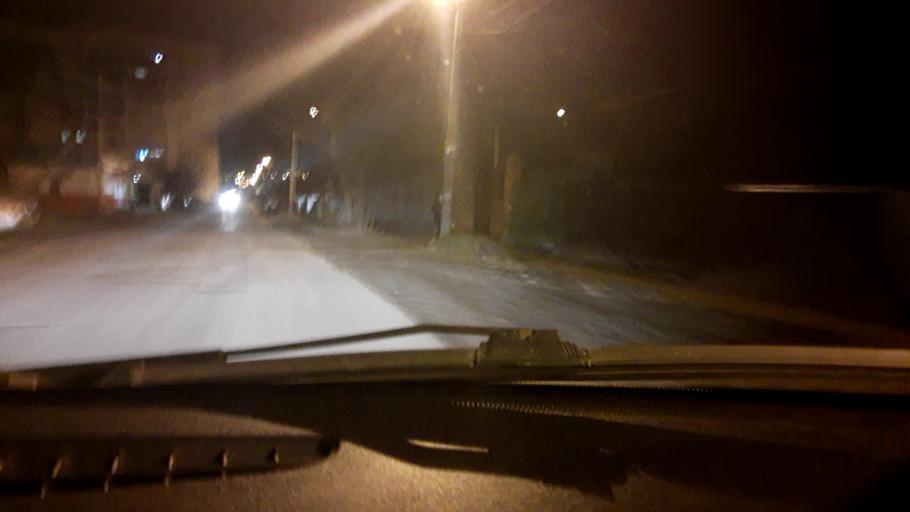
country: RU
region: Bashkortostan
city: Avdon
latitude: 54.6993
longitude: 55.8196
